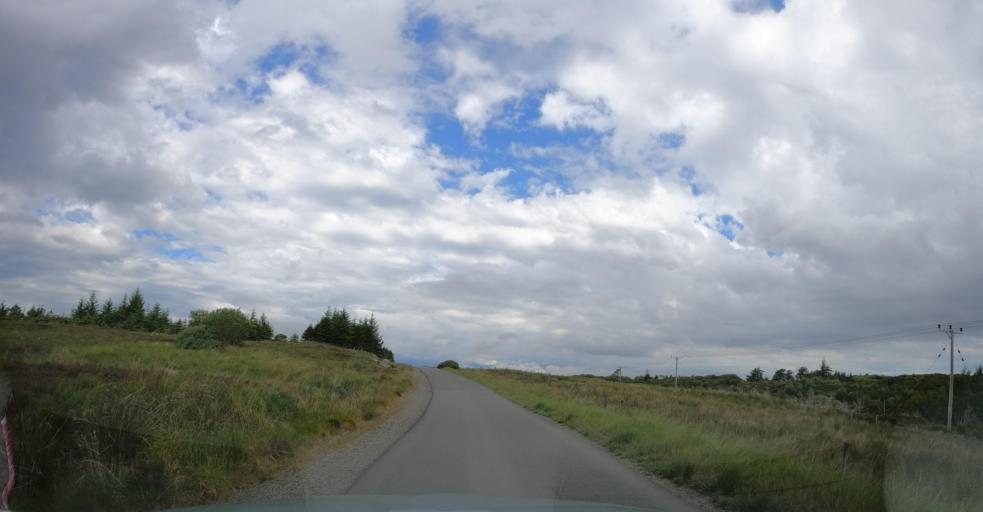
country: GB
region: Scotland
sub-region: Eilean Siar
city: Stornoway
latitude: 58.2028
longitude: -6.4133
